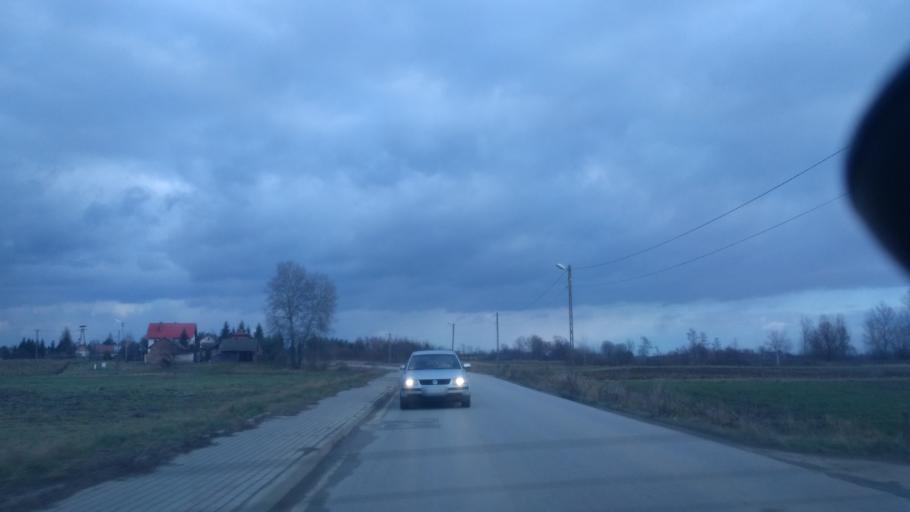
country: PL
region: Subcarpathian Voivodeship
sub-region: Powiat lancucki
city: Czarna
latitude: 50.1134
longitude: 22.2195
